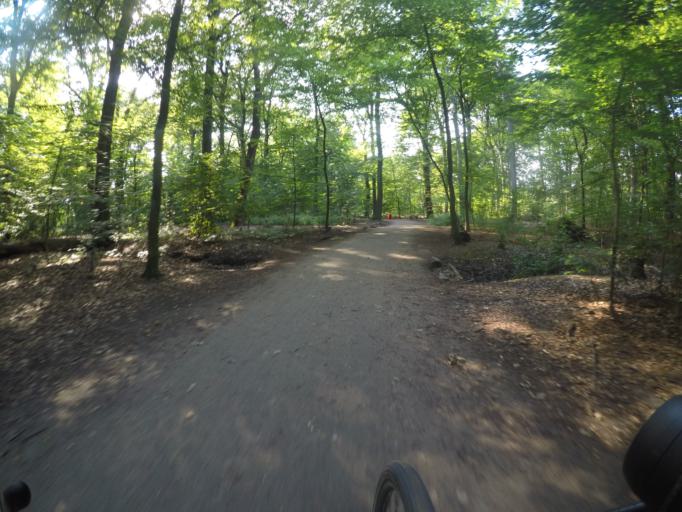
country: DE
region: Hamburg
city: Marienthal
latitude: 53.5679
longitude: 10.0882
